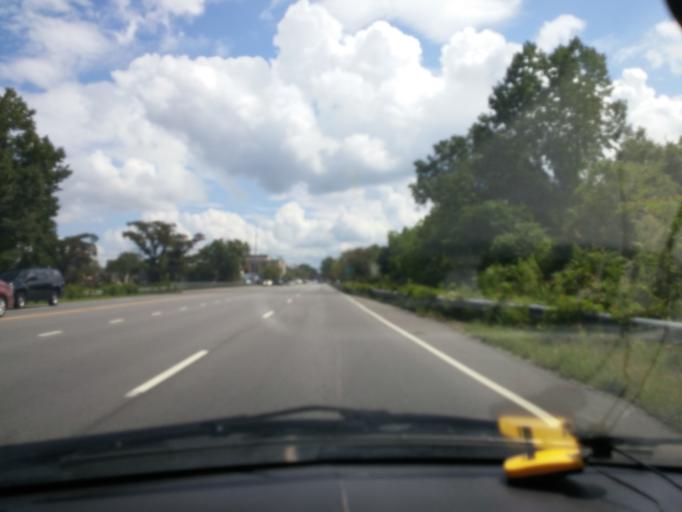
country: US
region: North Carolina
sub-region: Lenoir County
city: Kinston
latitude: 35.2588
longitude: -77.5849
